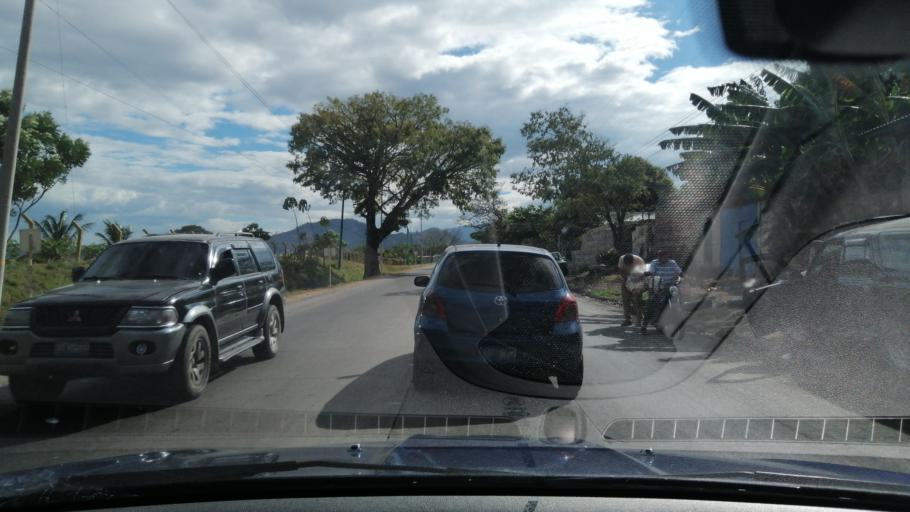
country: SV
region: Santa Ana
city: Santa Ana
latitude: 14.0388
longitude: -89.5215
